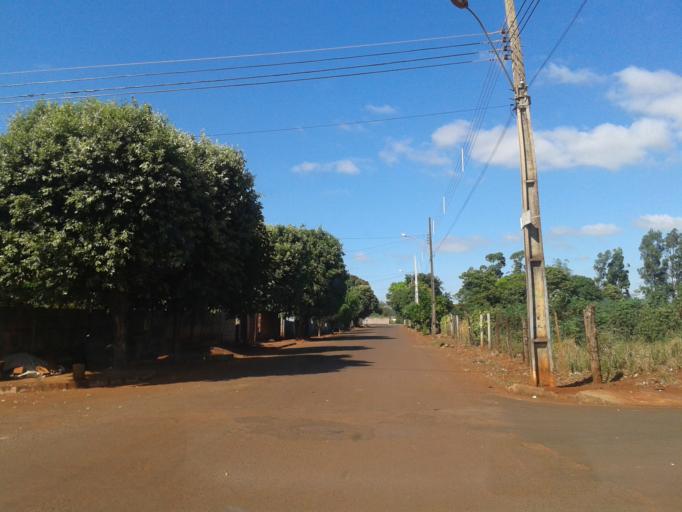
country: BR
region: Minas Gerais
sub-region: Centralina
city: Centralina
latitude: -18.5878
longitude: -49.2032
